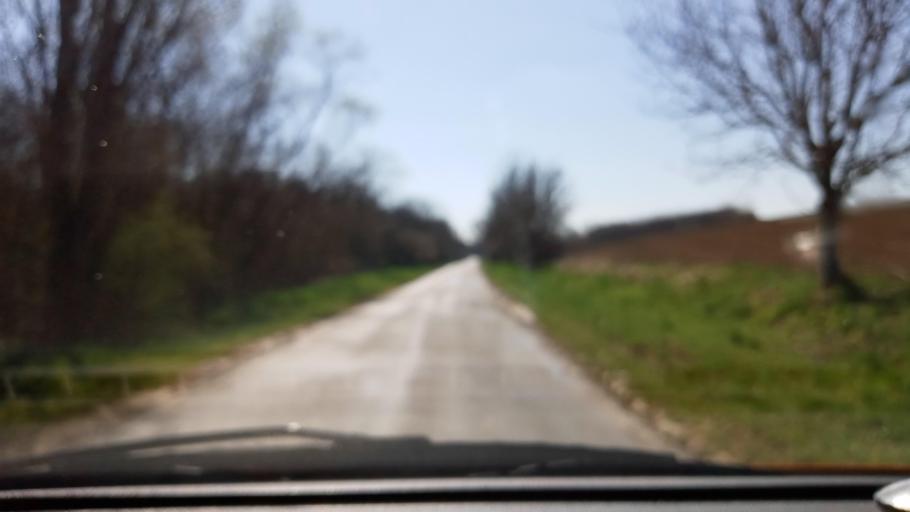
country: HU
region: Baranya
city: Kozarmisleny
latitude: 46.0712
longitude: 18.3642
